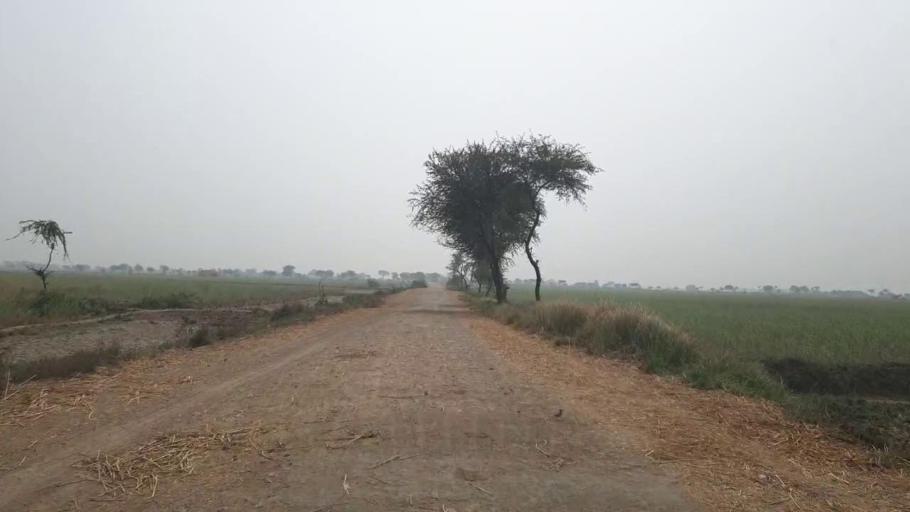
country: PK
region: Sindh
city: Kario
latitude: 24.6506
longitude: 68.6217
